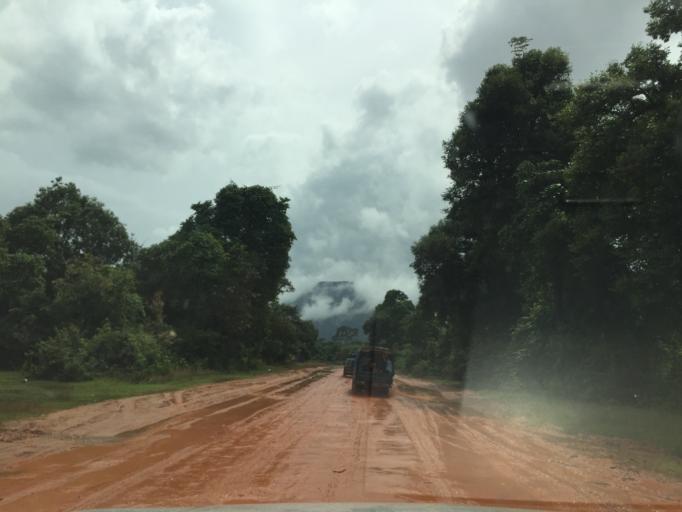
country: LA
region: Attapu
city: Attapu
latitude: 14.8079
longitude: 106.7720
